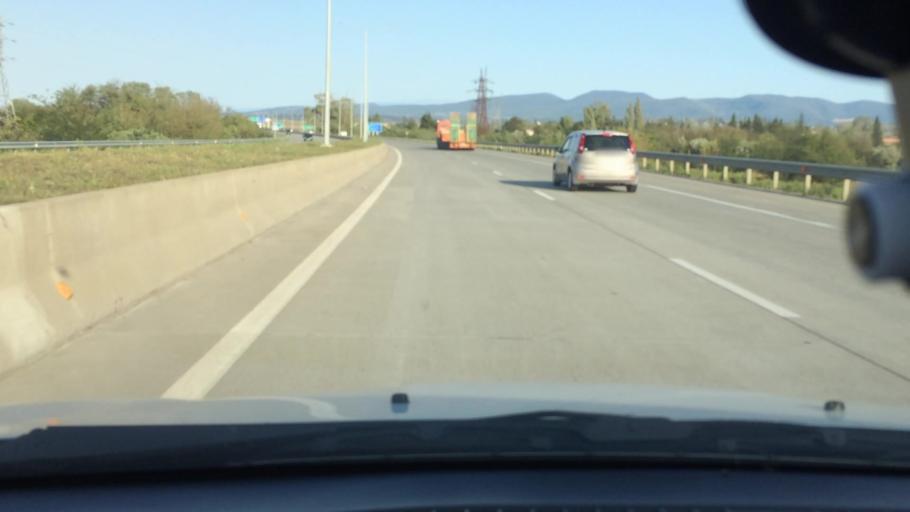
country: GE
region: Imereti
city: Zestap'oni
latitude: 42.1528
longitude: 42.9588
